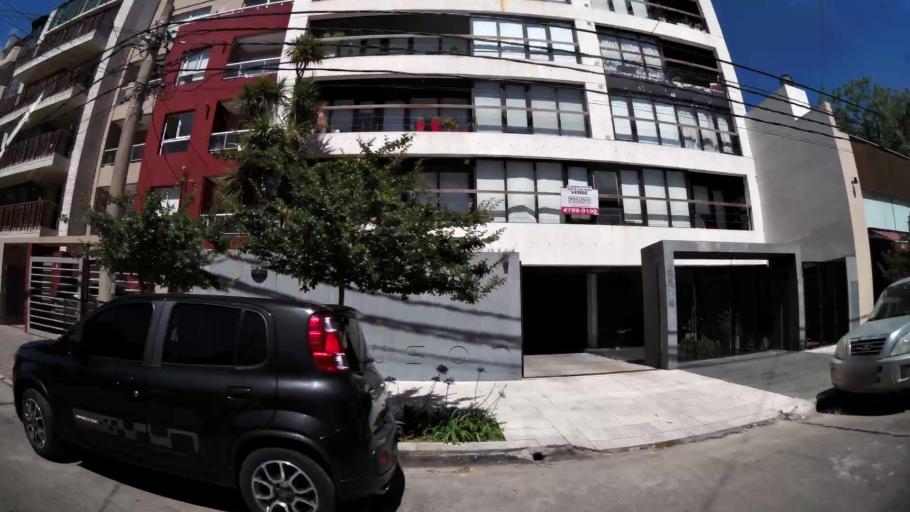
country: AR
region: Buenos Aires
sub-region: Partido de Vicente Lopez
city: Olivos
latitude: -34.4987
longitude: -58.4885
